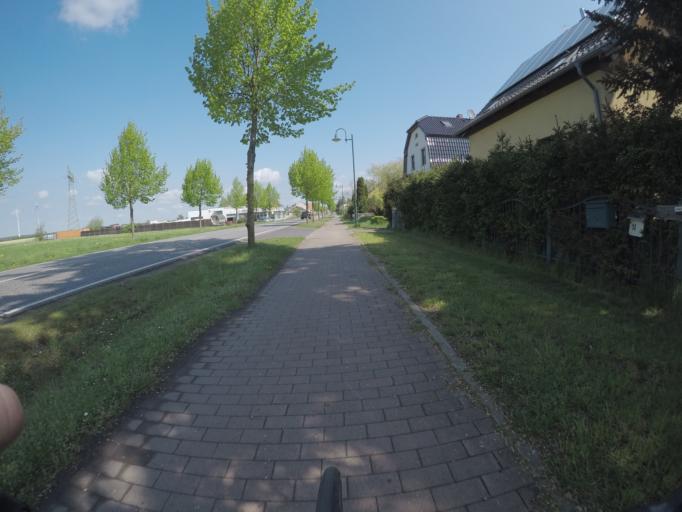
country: DE
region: Brandenburg
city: Wandlitz
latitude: 52.7817
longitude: 13.4796
